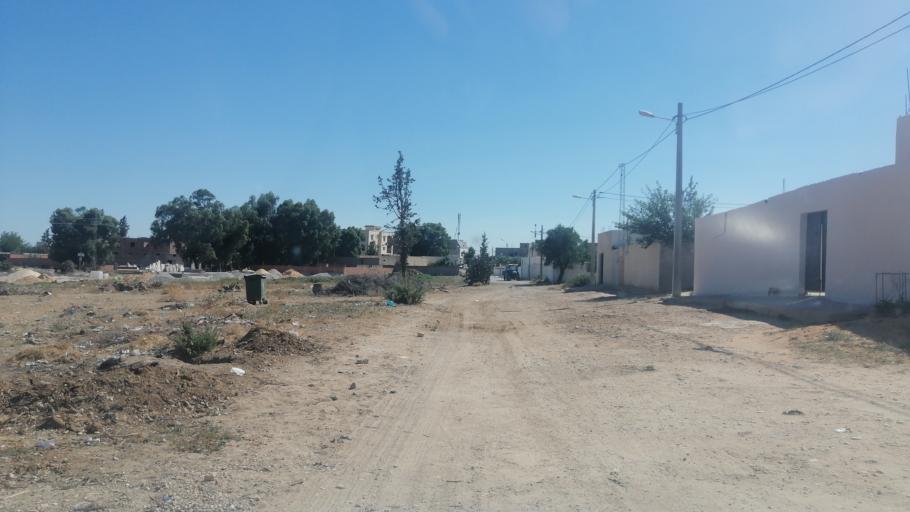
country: TN
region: Al Qayrawan
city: Sbikha
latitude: 36.1273
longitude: 10.0974
